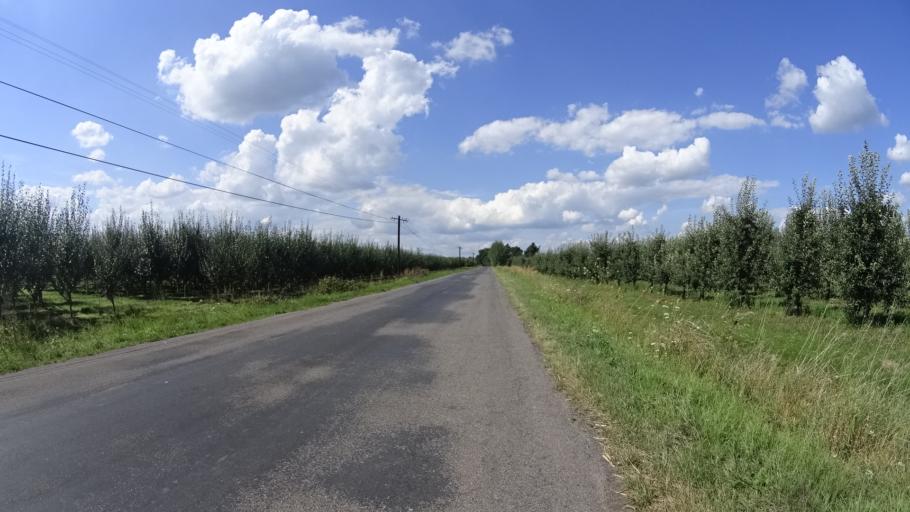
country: PL
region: Masovian Voivodeship
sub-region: Powiat grojecki
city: Mogielnica
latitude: 51.6876
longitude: 20.7524
